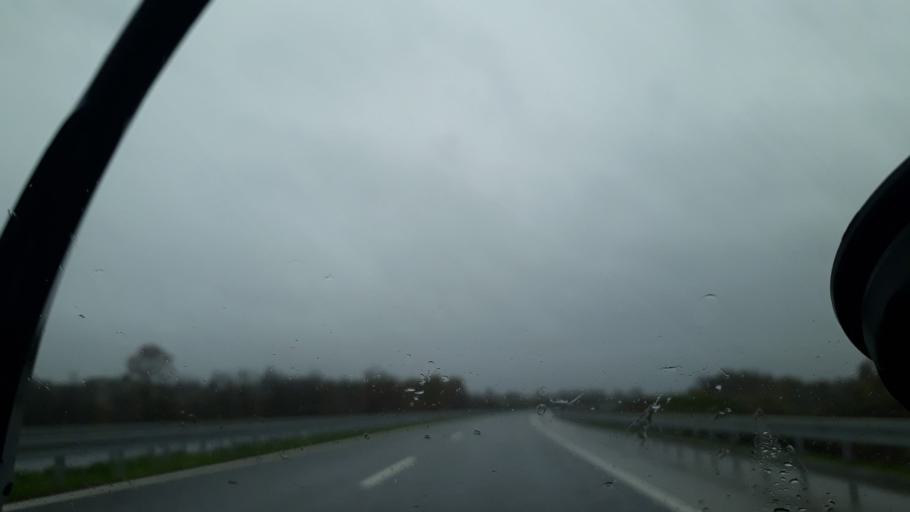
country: BA
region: Republika Srpska
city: Stanari
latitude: 44.8223
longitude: 17.8137
